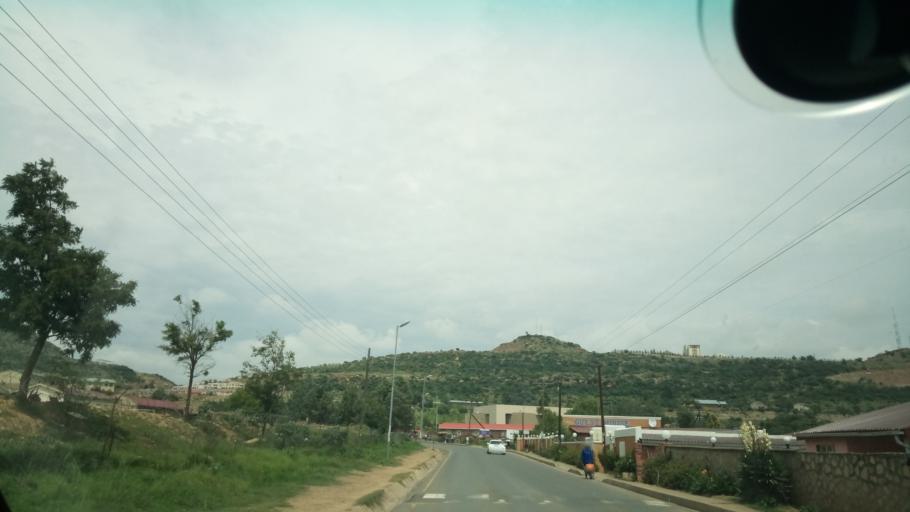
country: LS
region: Maseru
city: Maseru
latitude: -29.3223
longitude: 27.5024
